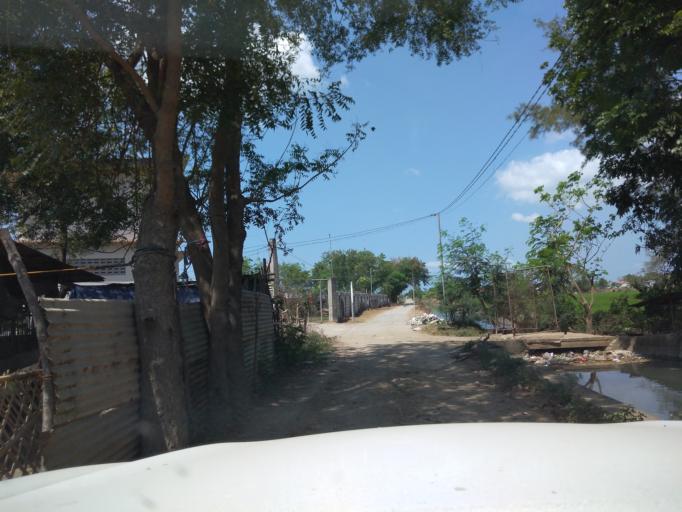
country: PH
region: Central Luzon
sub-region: Province of Pampanga
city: Bahay Pare
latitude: 15.0421
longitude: 120.8736
